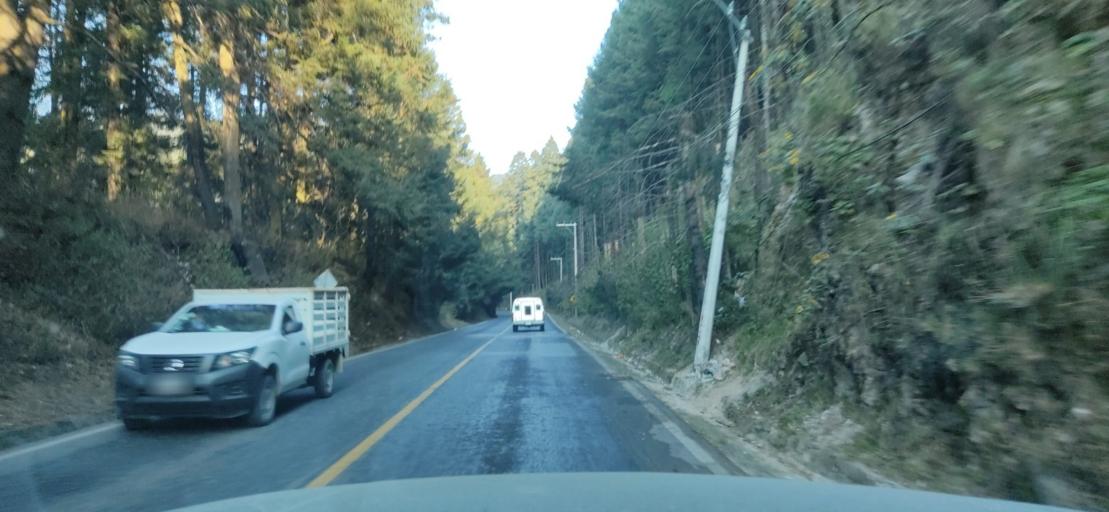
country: MX
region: Mexico
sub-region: Ocoyoacac
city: San Jeronimo Acazulco
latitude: 19.2609
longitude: -99.3743
